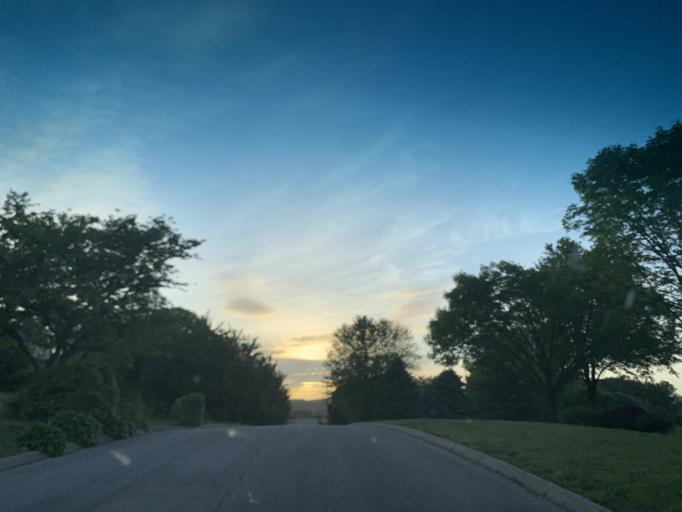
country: US
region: Maryland
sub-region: Harford County
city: South Bel Air
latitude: 39.5803
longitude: -76.2794
